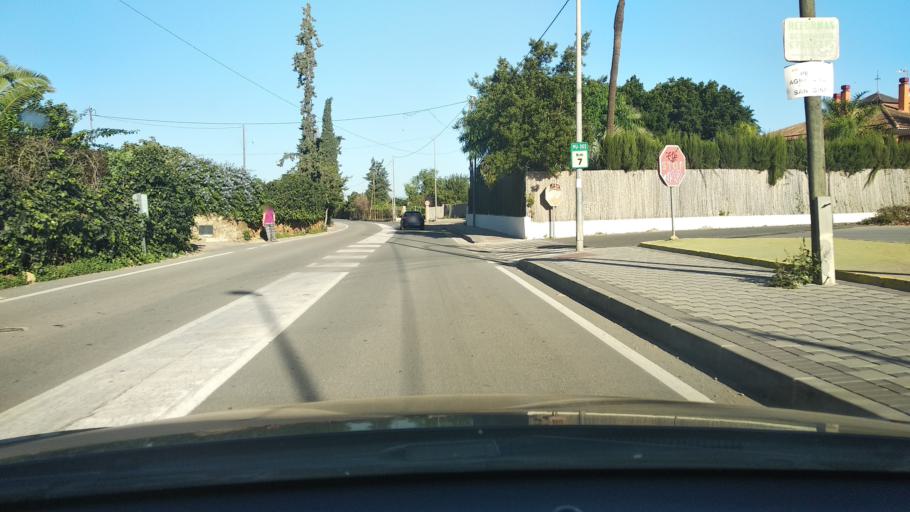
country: ES
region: Murcia
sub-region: Murcia
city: Murcia
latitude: 37.9434
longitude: -1.1192
